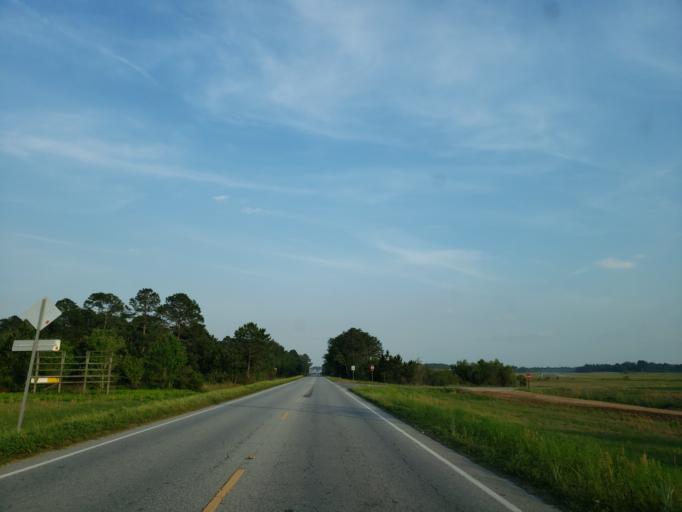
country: US
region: Georgia
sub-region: Cook County
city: Sparks
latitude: 31.1460
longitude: -83.4577
